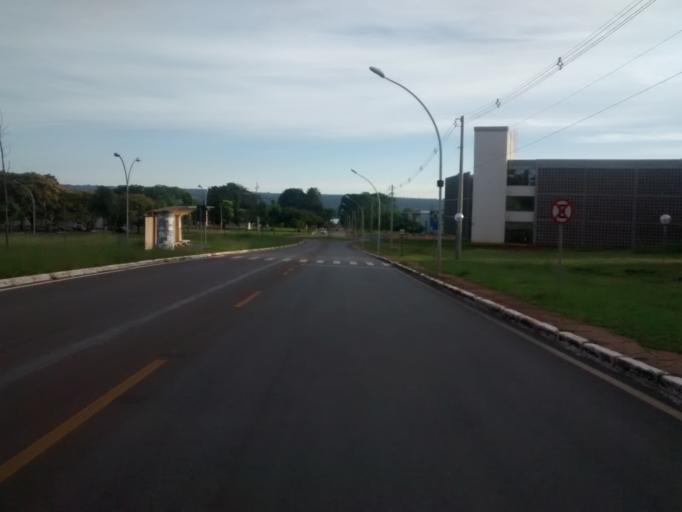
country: BR
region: Federal District
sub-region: Brasilia
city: Brasilia
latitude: -15.7676
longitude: -47.8678
